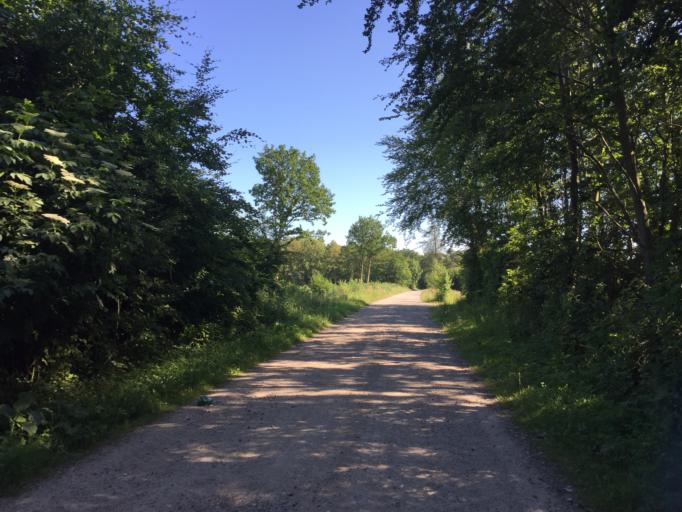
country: DK
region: South Denmark
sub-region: Kerteminde Kommune
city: Langeskov
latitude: 55.3670
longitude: 10.5496
